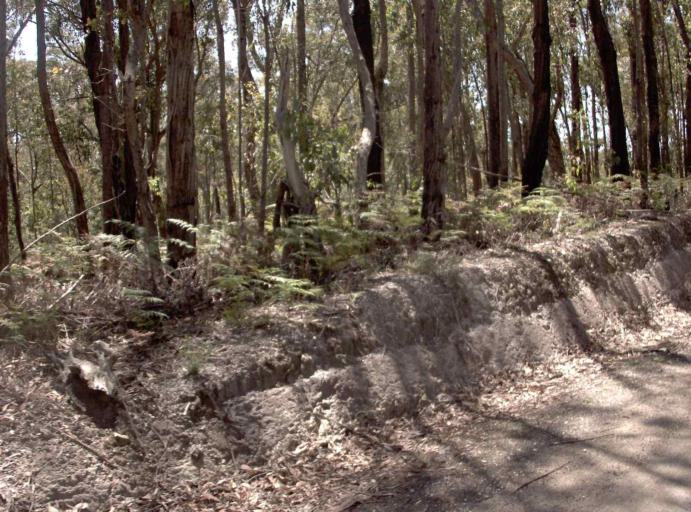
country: AU
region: Victoria
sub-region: East Gippsland
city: Lakes Entrance
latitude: -37.6964
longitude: 148.7331
